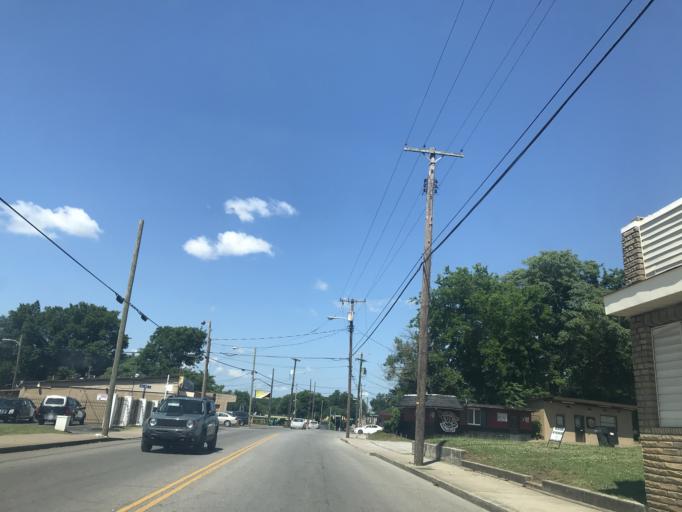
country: US
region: Tennessee
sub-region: Davidson County
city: Nashville
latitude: 36.1801
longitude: -86.8088
